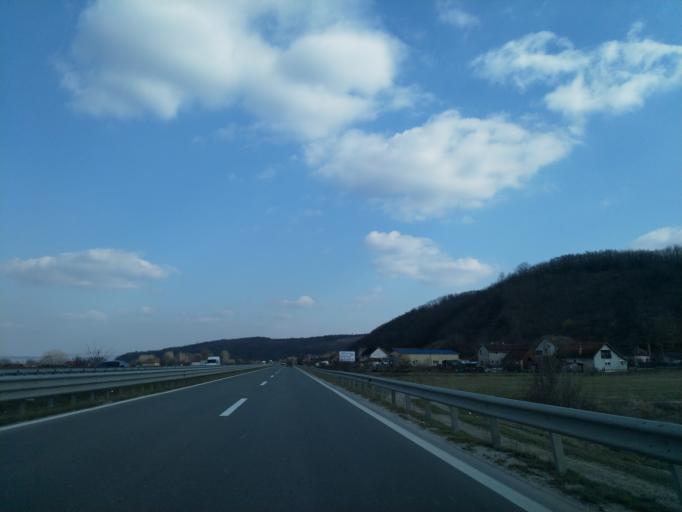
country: RS
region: Central Serbia
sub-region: Sumadijski Okrug
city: Batocina
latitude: 44.1491
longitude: 21.0435
